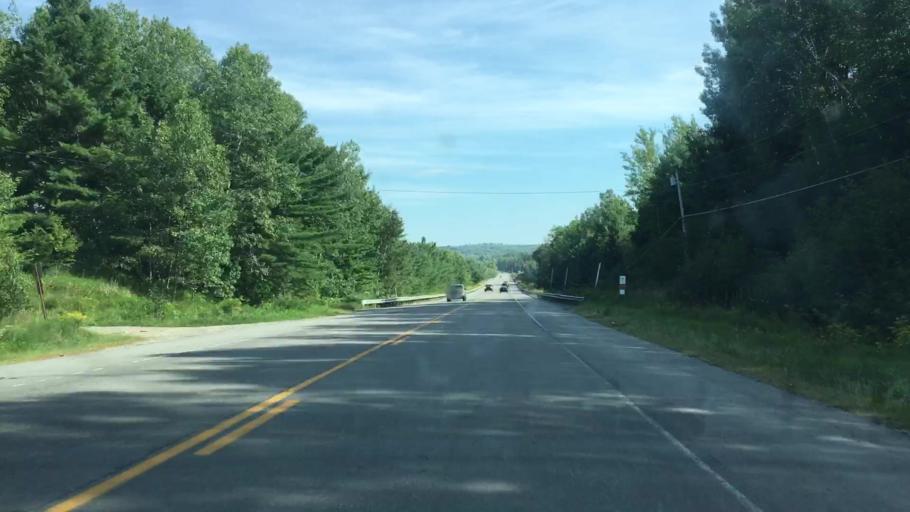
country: US
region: Maine
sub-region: Penobscot County
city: Lincoln
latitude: 45.3677
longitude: -68.5534
